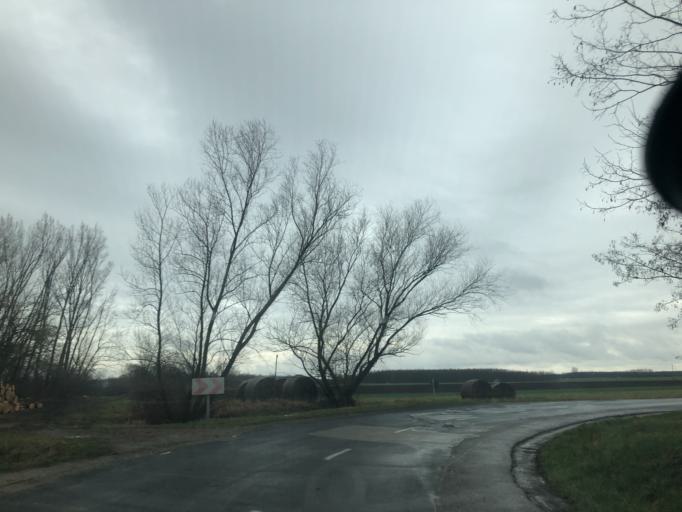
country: HU
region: Gyor-Moson-Sopron
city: Fertoszentmiklos
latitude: 47.6071
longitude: 16.9359
